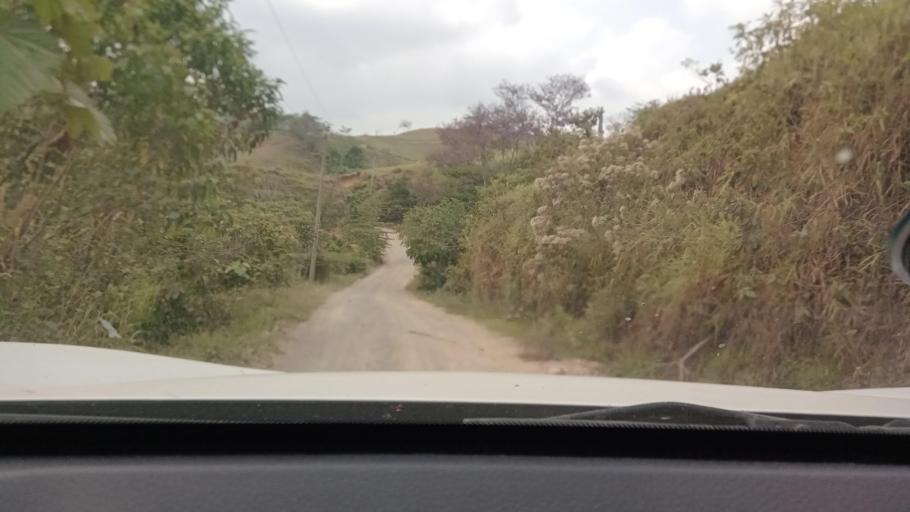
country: MX
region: Tabasco
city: Chontalpa
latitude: 17.5024
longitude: -93.6441
